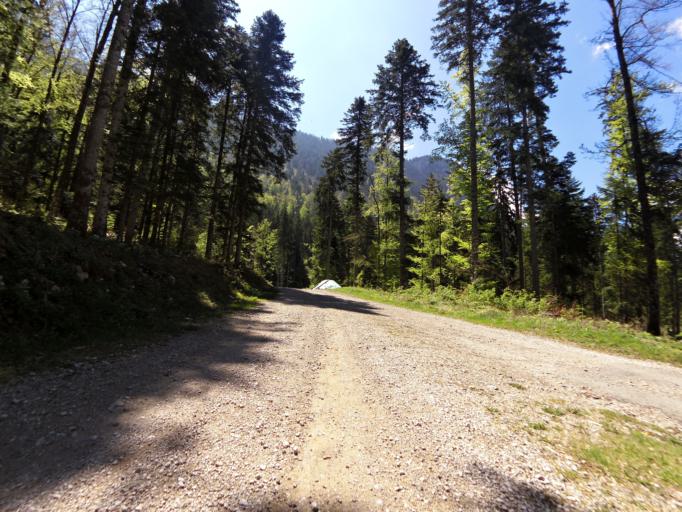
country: CH
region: Vaud
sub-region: Jura-Nord vaudois District
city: Vallorbe
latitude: 46.6955
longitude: 6.3550
